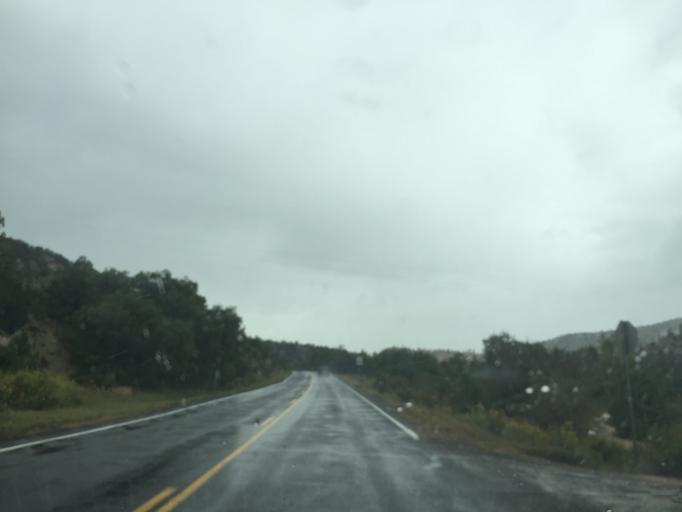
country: US
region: Utah
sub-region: Garfield County
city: Panguitch
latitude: 37.6575
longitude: -112.0919
